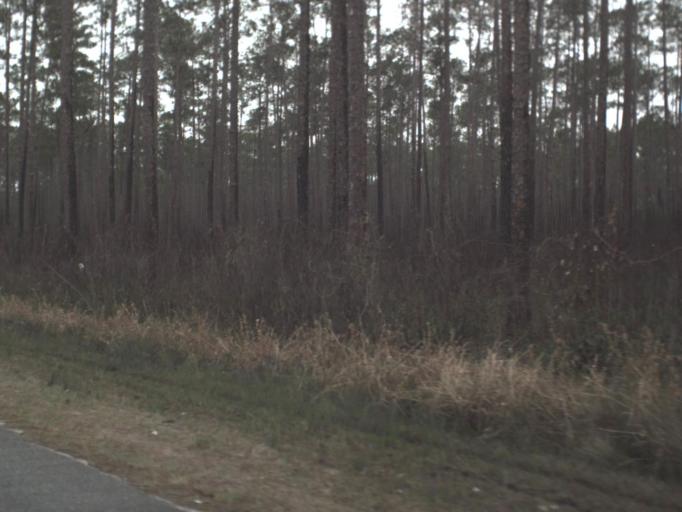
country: US
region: Florida
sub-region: Franklin County
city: Apalachicola
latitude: 29.9474
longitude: -84.9765
